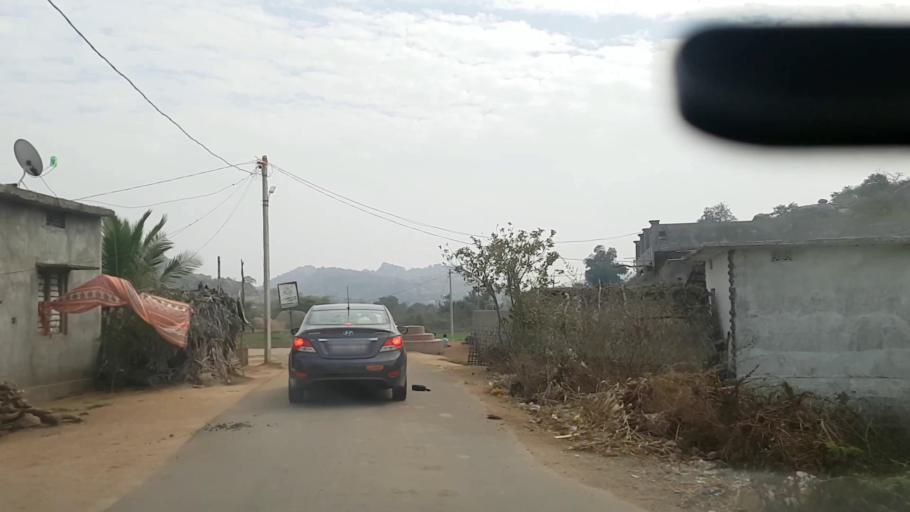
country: IN
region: Telangana
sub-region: Rangareddi
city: Lal Bahadur Nagar
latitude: 17.1800
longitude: 78.7816
